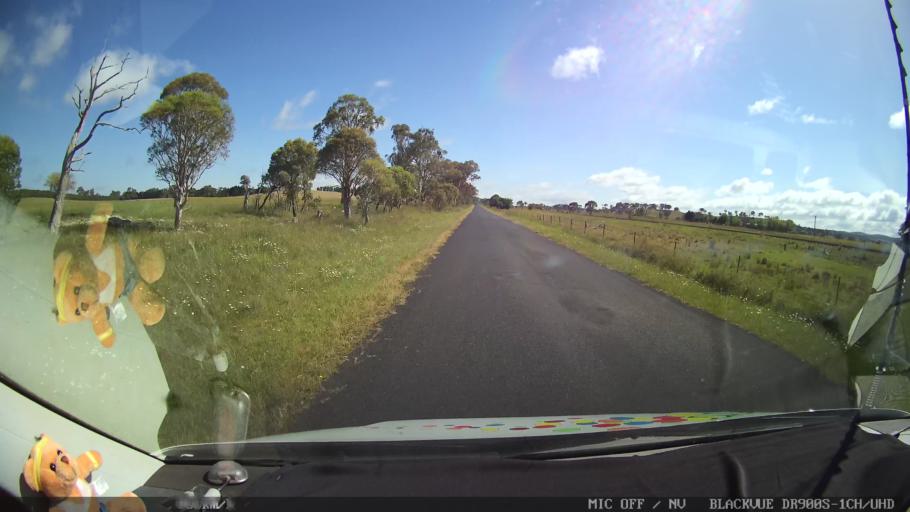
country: AU
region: New South Wales
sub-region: Guyra
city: Guyra
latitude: -30.1810
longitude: 151.6806
